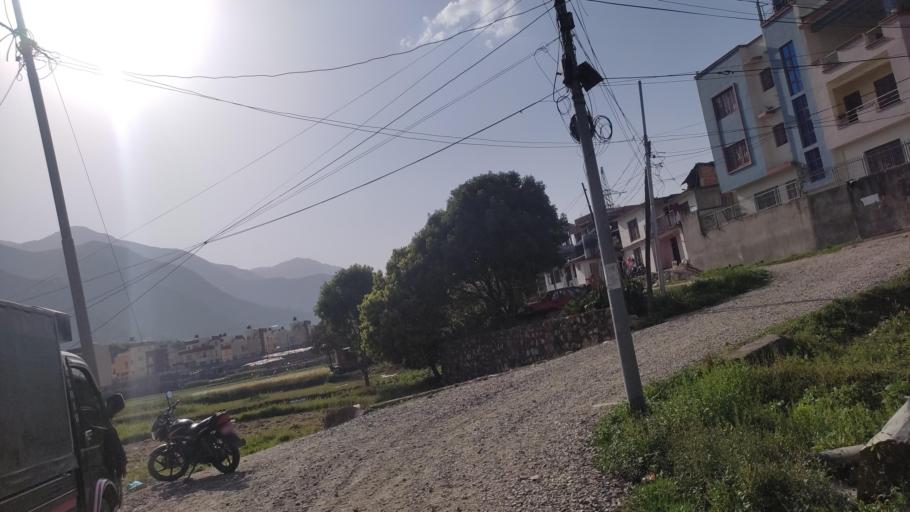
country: NP
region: Central Region
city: Kirtipur
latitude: 27.6562
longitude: 85.2847
